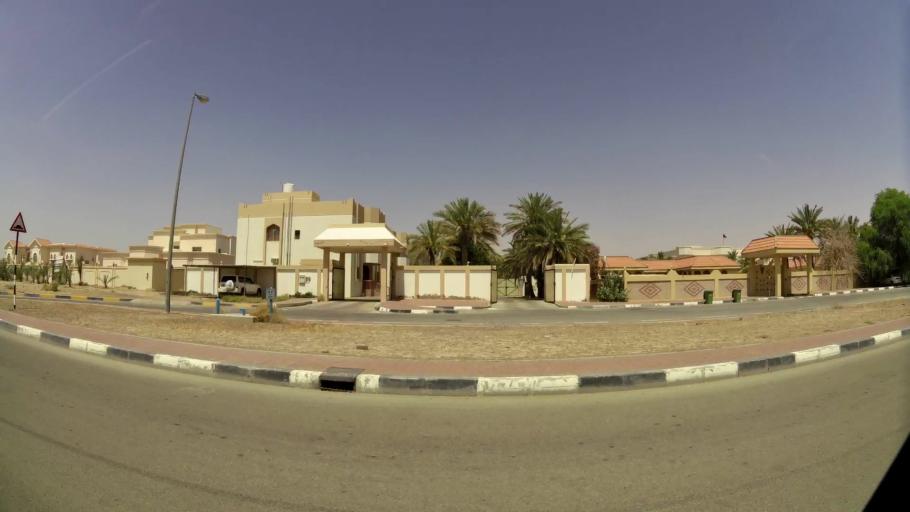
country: OM
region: Al Buraimi
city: Al Buraymi
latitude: 24.2816
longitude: 55.7611
